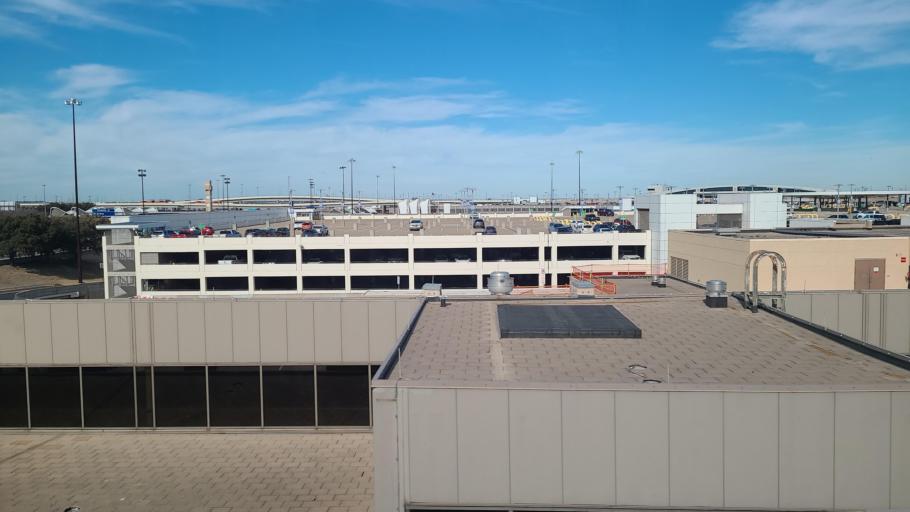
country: US
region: Texas
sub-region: Tarrant County
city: Grapevine
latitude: 32.9021
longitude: -97.0383
